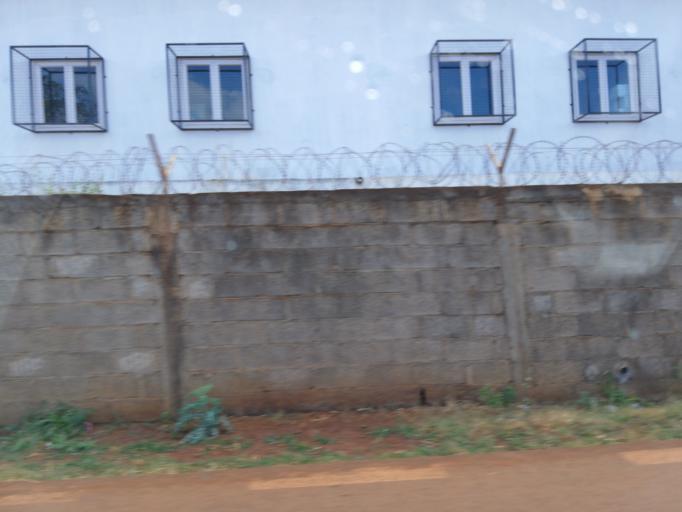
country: MU
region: Black River
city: Petite Riviere
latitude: -20.1923
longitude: 57.4652
